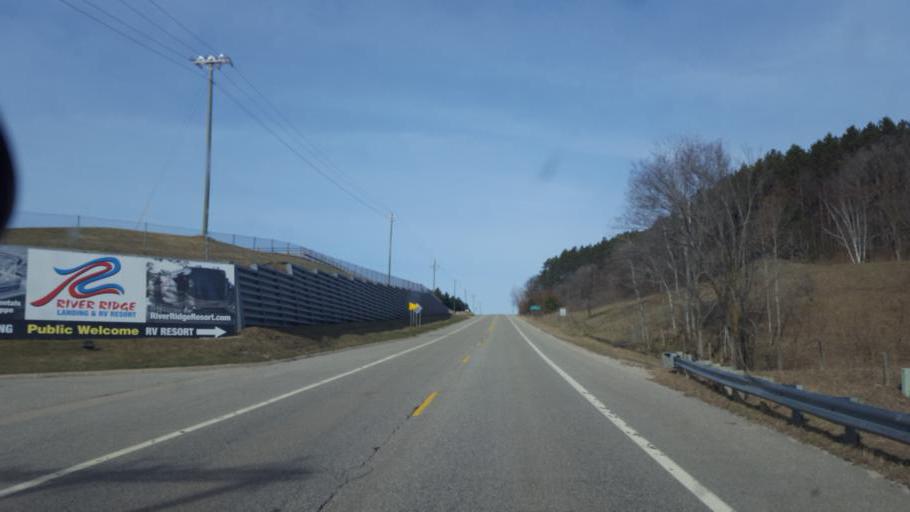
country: US
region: Michigan
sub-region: Mecosta County
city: Big Rapids
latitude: 43.5840
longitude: -85.5275
